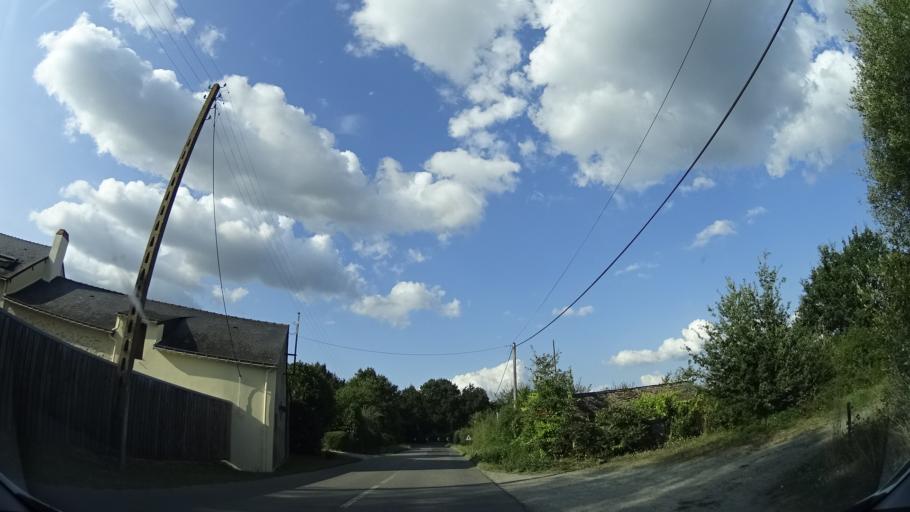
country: FR
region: Pays de la Loire
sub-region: Departement de la Loire-Atlantique
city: Suce-sur-Erdre
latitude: 47.3693
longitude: -1.5222
